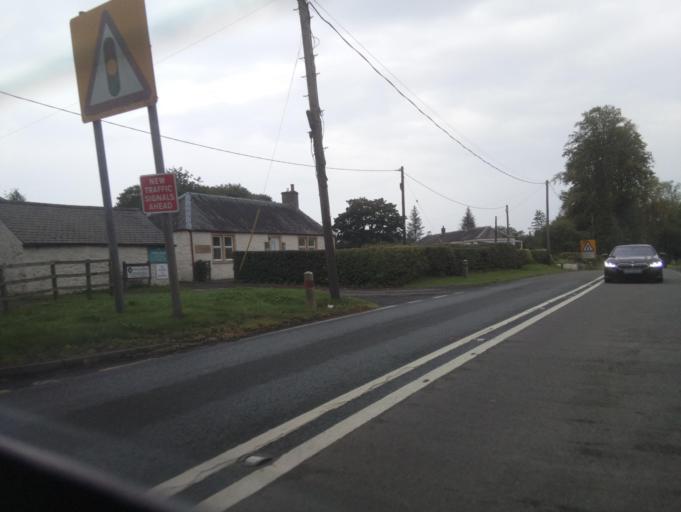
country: GB
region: Scotland
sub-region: Dumfries and Galloway
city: Lochmaben
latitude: 55.2268
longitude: -3.4637
